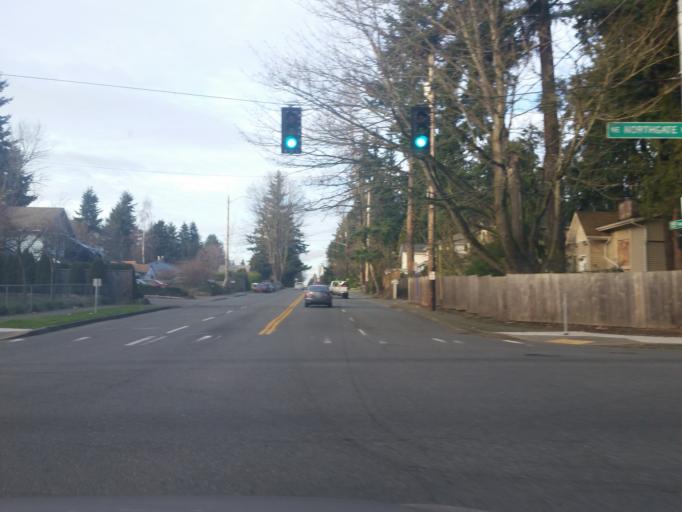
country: US
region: Washington
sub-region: King County
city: Shoreline
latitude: 47.7085
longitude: -122.3125
